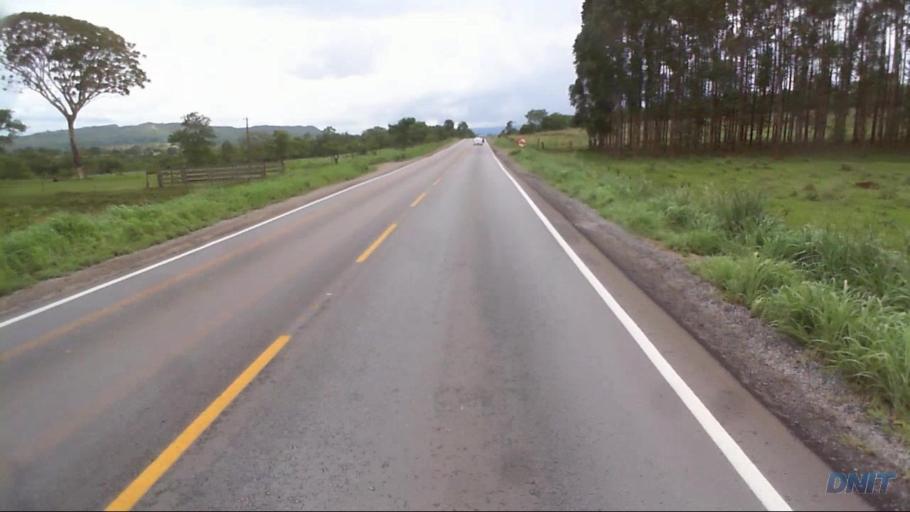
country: BR
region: Goias
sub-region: Padre Bernardo
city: Padre Bernardo
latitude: -15.5041
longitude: -48.2027
